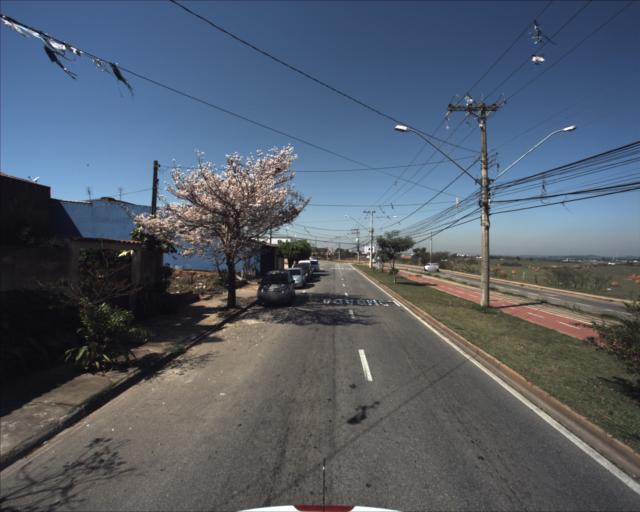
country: BR
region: Sao Paulo
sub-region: Sorocaba
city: Sorocaba
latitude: -23.4994
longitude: -47.5272
